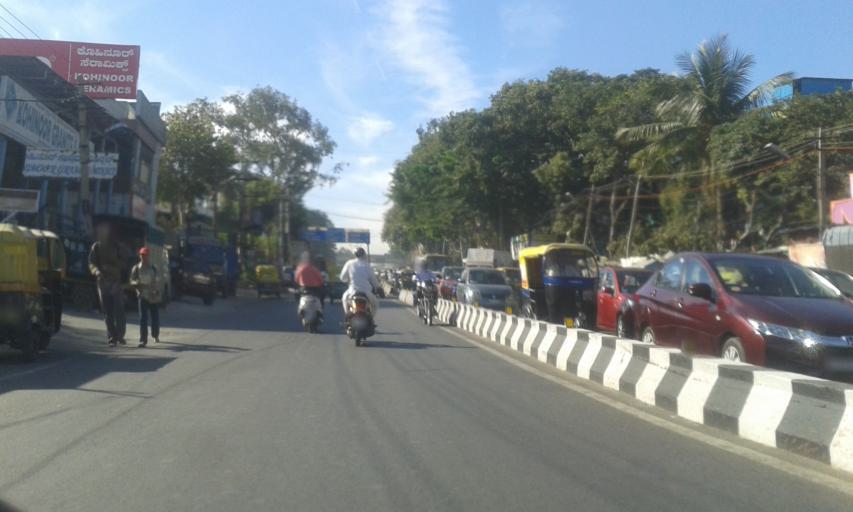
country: IN
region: Karnataka
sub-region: Bangalore Urban
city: Bangalore
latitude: 12.9411
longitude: 77.6025
